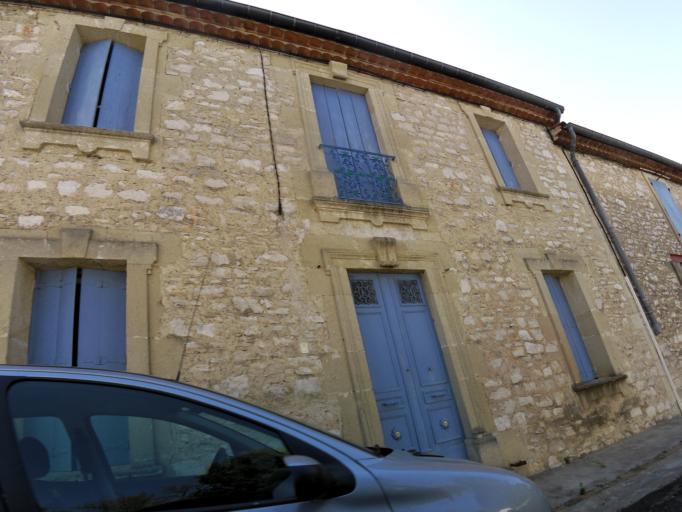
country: FR
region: Languedoc-Roussillon
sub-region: Departement du Gard
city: Sommieres
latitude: 43.8066
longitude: 4.0706
